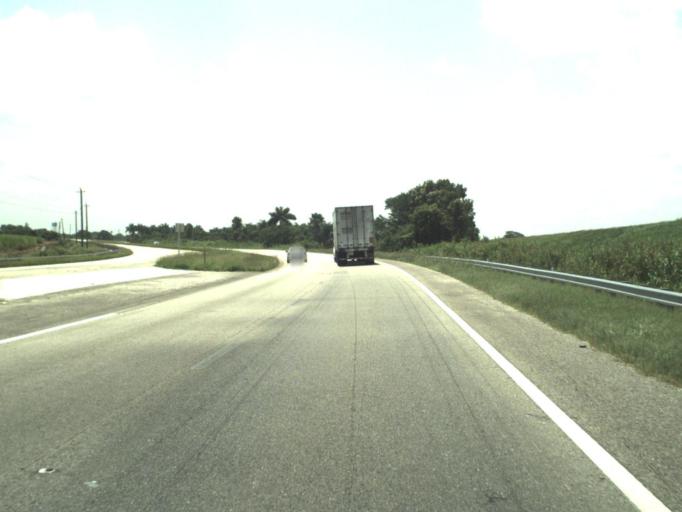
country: US
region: Florida
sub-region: Palm Beach County
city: South Bay
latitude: 26.6982
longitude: -80.7957
